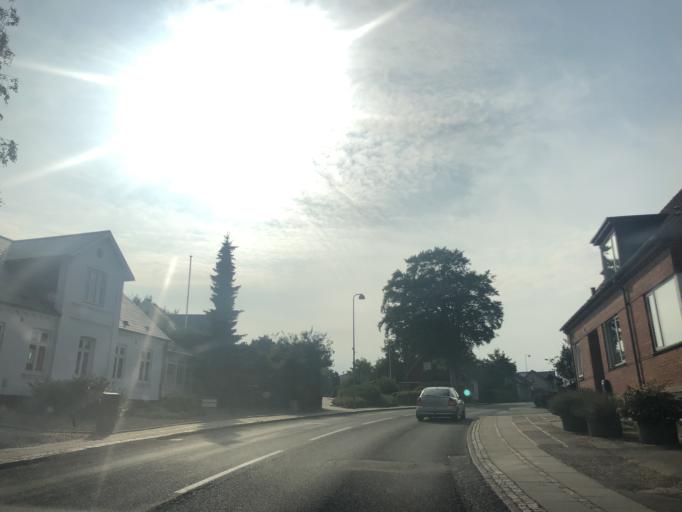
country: DK
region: Central Jutland
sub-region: Skive Kommune
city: Skive
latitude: 56.7010
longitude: 8.9881
